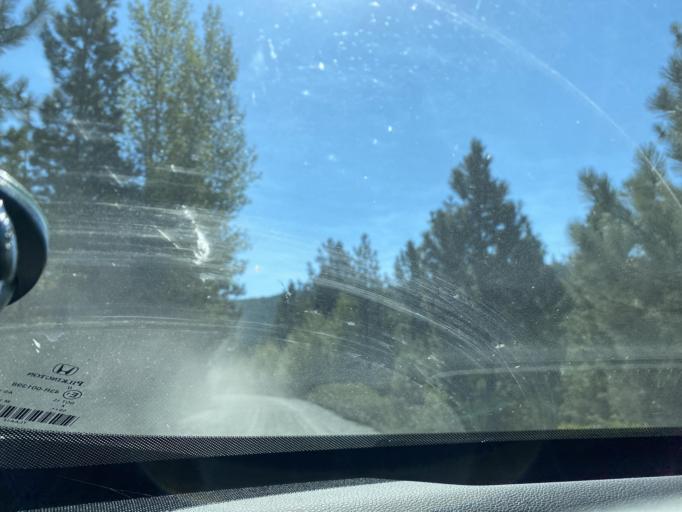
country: US
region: Oregon
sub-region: Deschutes County
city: Sunriver
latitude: 44.0309
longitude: -121.5618
